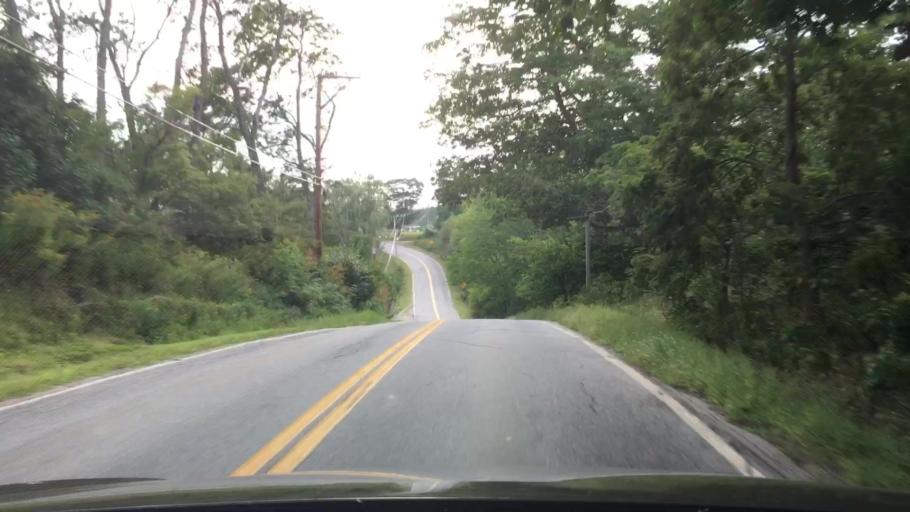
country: US
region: Maine
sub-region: Hancock County
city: Penobscot
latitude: 44.4718
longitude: -68.7356
